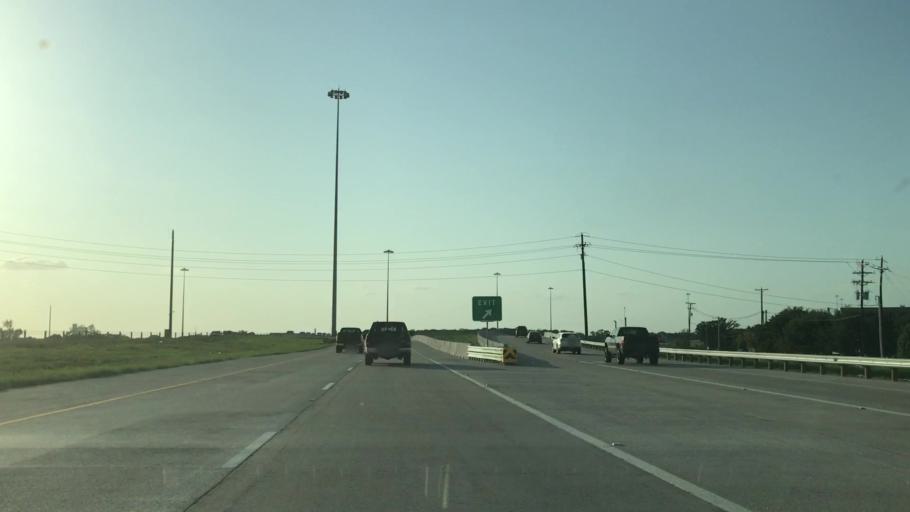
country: US
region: Texas
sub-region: Tarrant County
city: Grapevine
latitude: 32.9021
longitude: -97.0953
